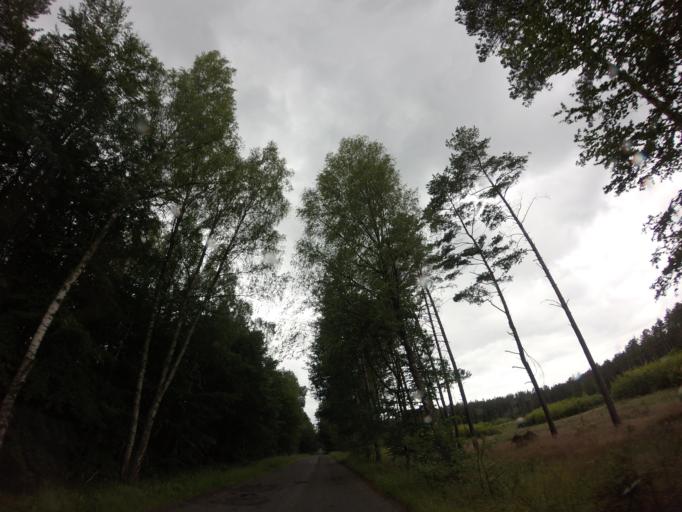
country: PL
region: West Pomeranian Voivodeship
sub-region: Powiat stargardzki
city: Insko
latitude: 53.4643
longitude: 15.6736
